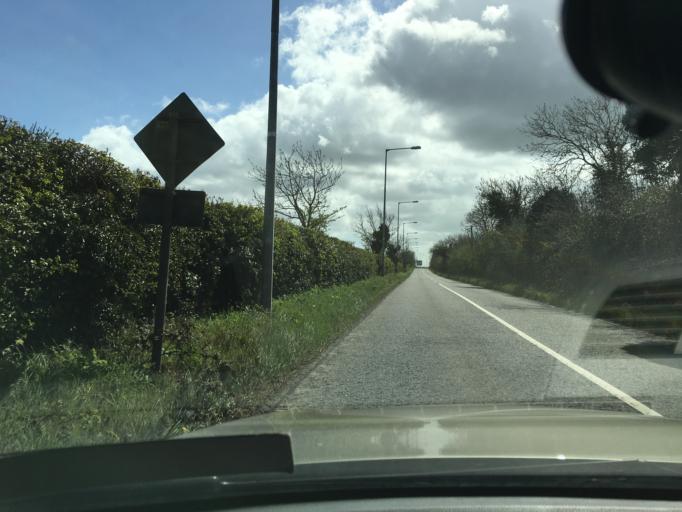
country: IE
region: Leinster
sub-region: Fingal County
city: Blanchardstown
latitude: 53.4264
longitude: -6.3691
